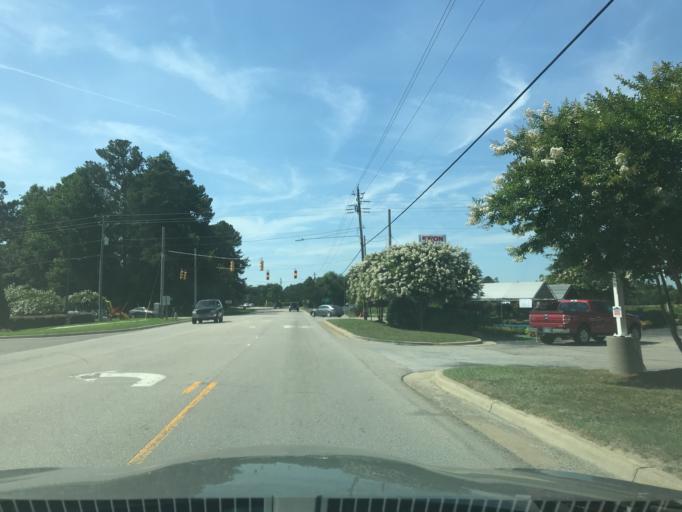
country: US
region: North Carolina
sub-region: Wake County
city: Wendell
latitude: 35.7921
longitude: -78.3786
